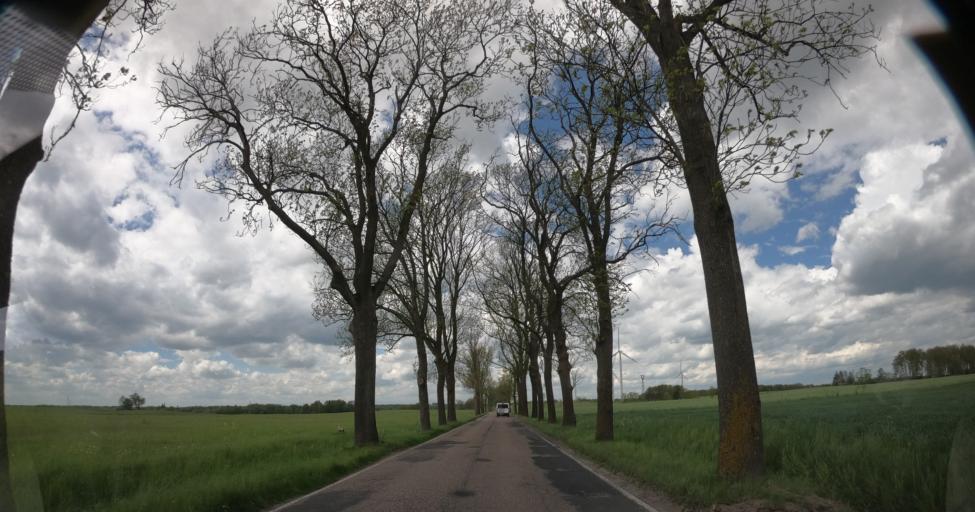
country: PL
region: West Pomeranian Voivodeship
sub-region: Powiat drawski
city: Drawsko Pomorskie
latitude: 53.5464
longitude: 15.7888
